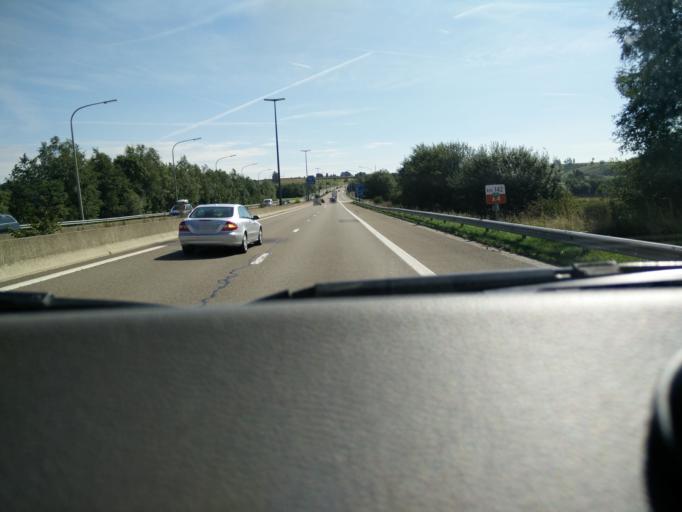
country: BE
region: Wallonia
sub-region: Province du Luxembourg
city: Neufchateau
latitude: 49.8754
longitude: 5.4768
